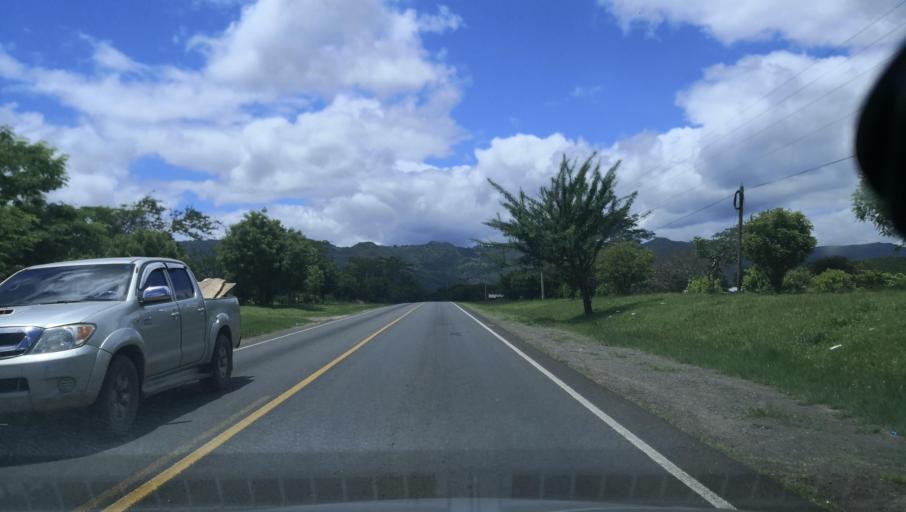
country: NI
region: Esteli
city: Condega
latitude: 13.2492
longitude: -86.3667
